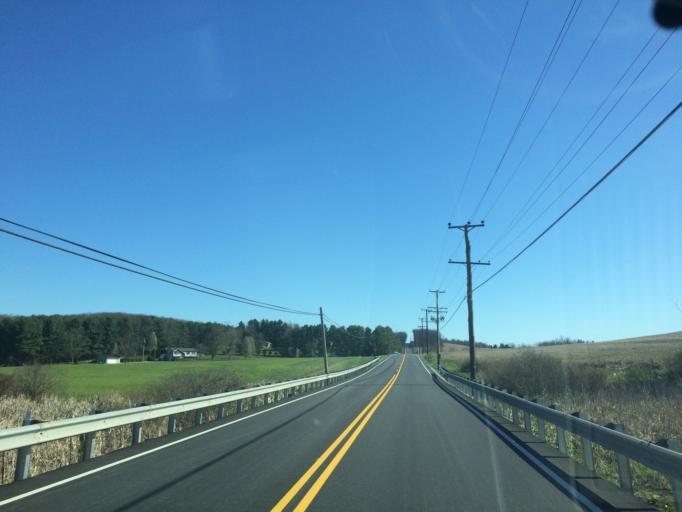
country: US
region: Maryland
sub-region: Carroll County
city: Westminster
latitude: 39.6338
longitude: -76.9888
